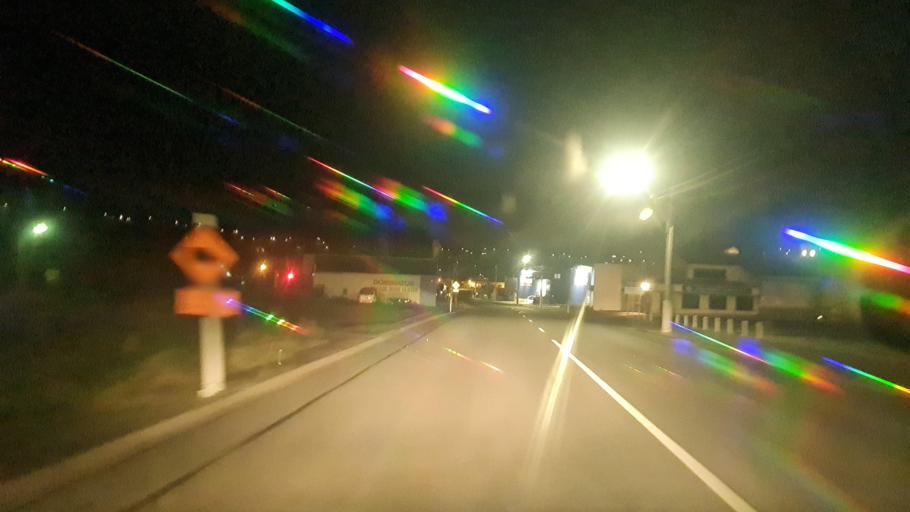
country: NZ
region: Otago
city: Oamaru
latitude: -45.0992
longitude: 170.9724
